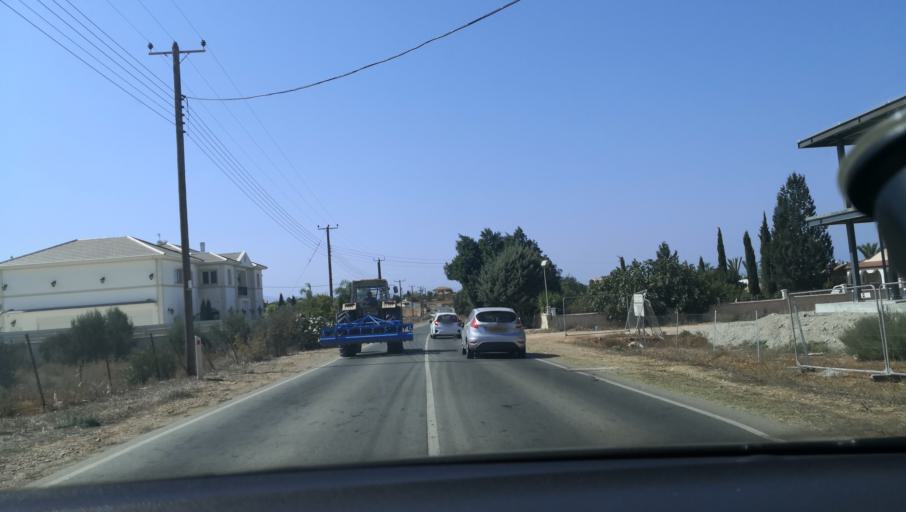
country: CY
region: Lefkosia
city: Pano Deftera
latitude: 35.1179
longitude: 33.2357
